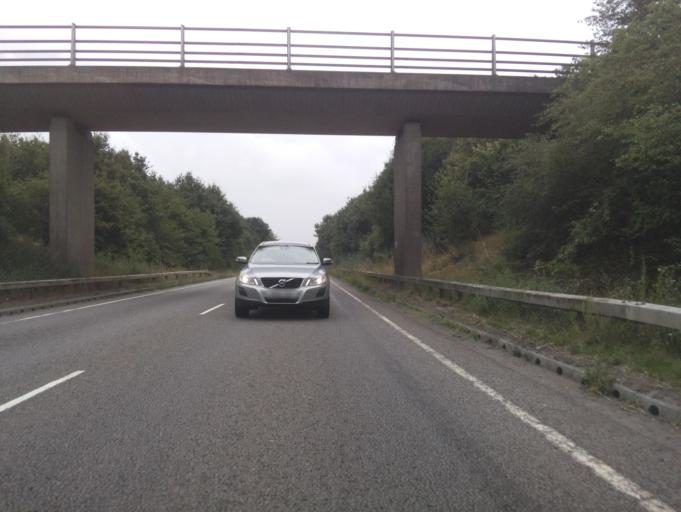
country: GB
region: England
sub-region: Nottinghamshire
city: South Collingham
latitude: 53.0928
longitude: -0.7703
